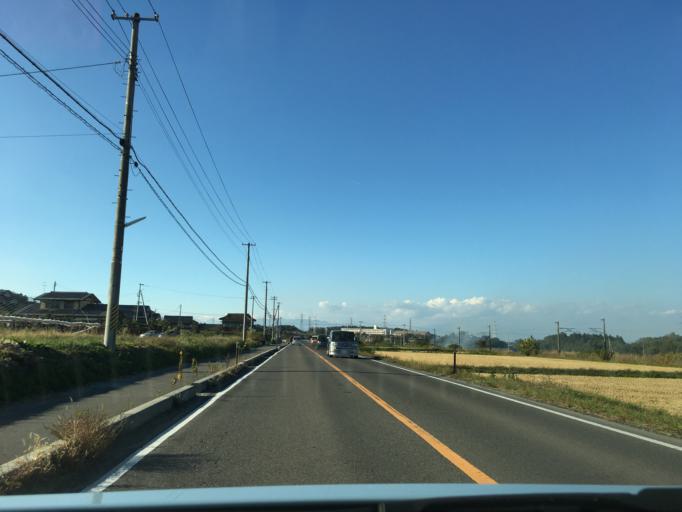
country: JP
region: Fukushima
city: Sukagawa
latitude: 37.3228
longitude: 140.3765
